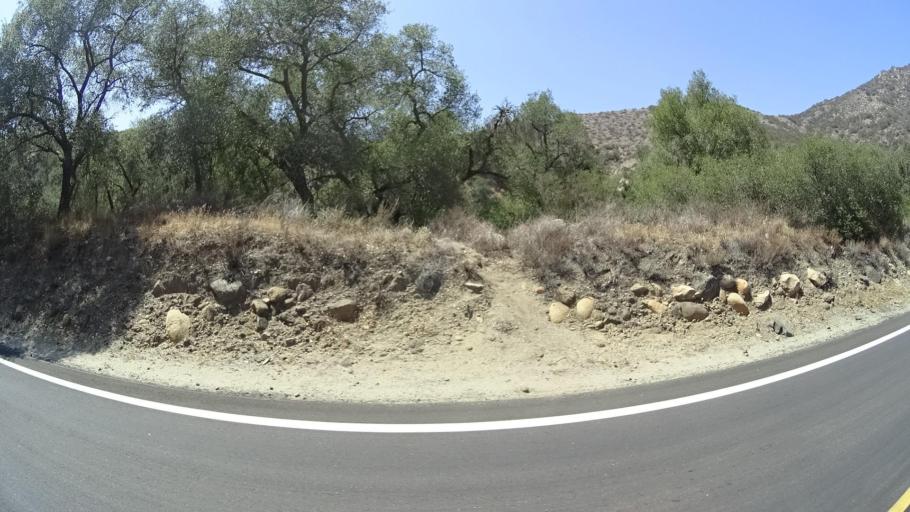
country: US
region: California
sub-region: San Diego County
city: Fallbrook
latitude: 33.3997
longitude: -117.2625
